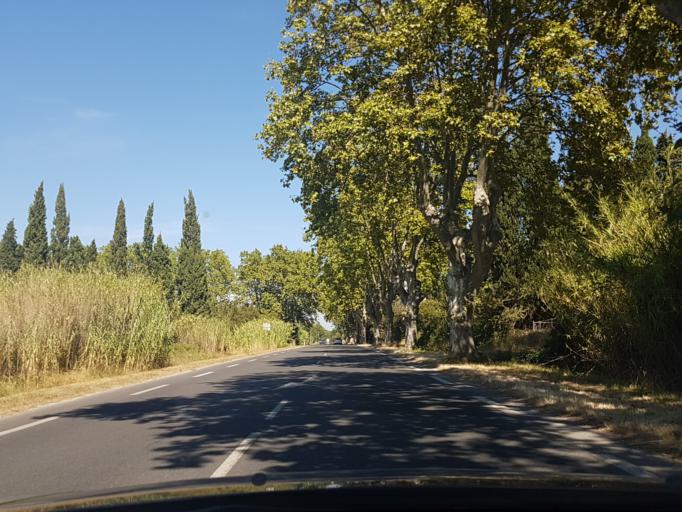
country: FR
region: Provence-Alpes-Cote d'Azur
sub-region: Departement des Bouches-du-Rhone
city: Saint-Remy-de-Provence
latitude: 43.8042
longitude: 4.8329
